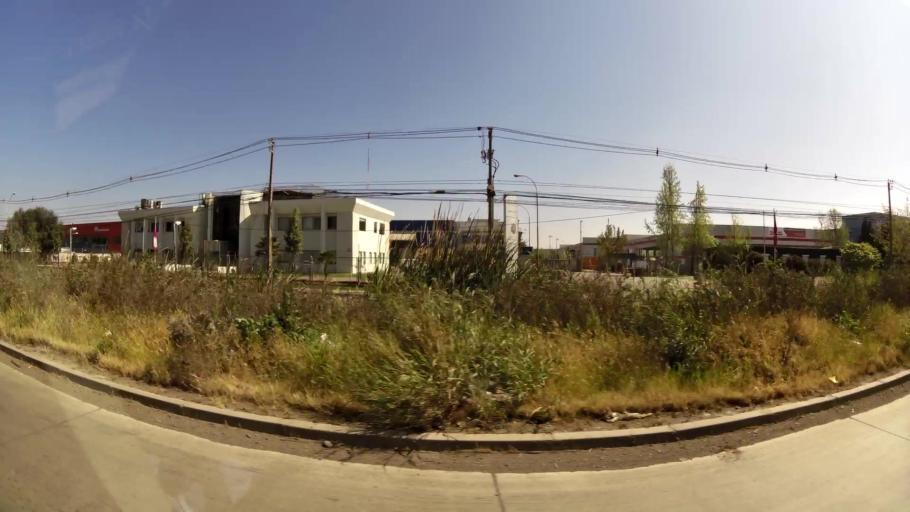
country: CL
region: Santiago Metropolitan
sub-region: Provincia de Chacabuco
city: Chicureo Abajo
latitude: -33.3171
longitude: -70.7310
